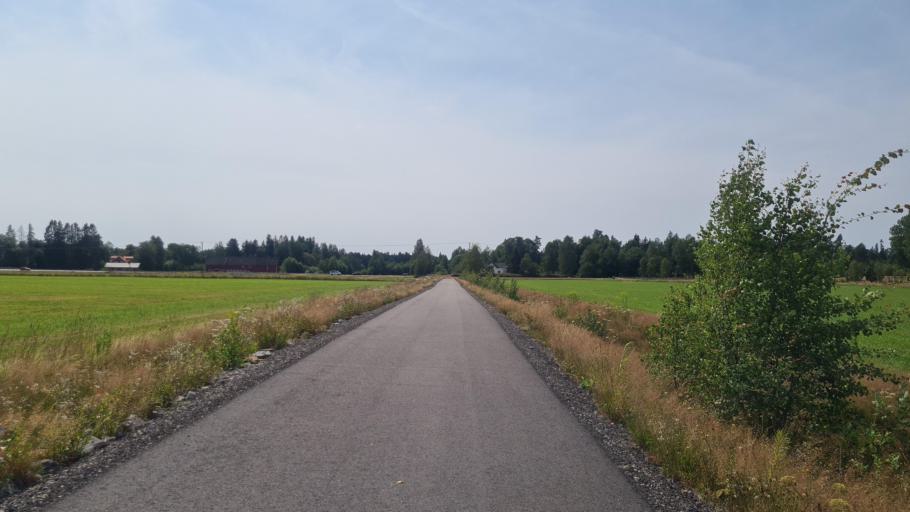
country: SE
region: Kronoberg
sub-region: Ljungby Kommun
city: Ljungby
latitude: 56.8539
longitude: 13.9714
